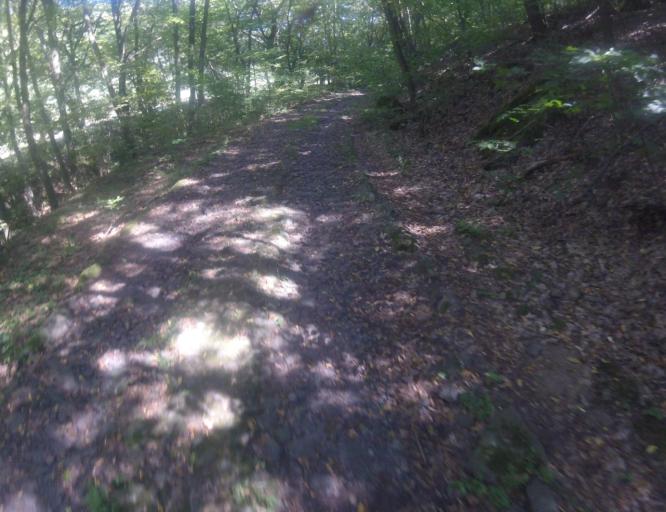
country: HU
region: Nograd
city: Bujak
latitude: 47.9386
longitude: 19.6063
